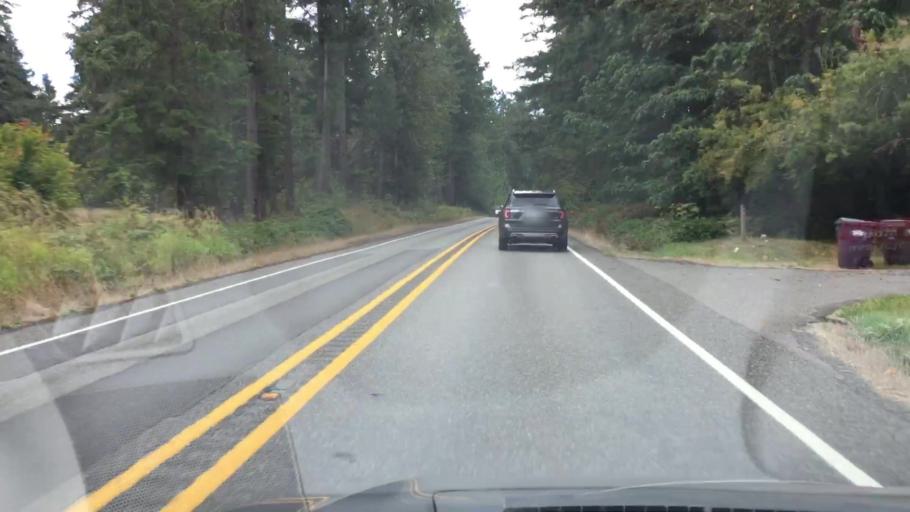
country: US
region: Washington
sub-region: Pierce County
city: Eatonville
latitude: 46.9162
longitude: -122.2913
